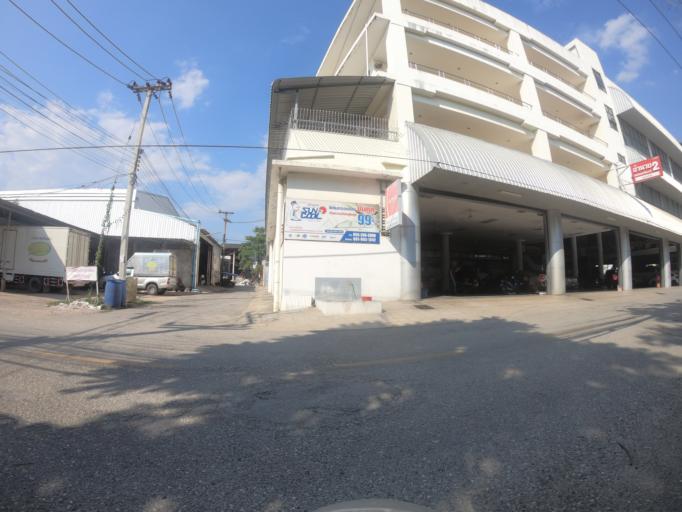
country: TH
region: Chiang Mai
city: Chiang Mai
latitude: 18.7890
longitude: 99.0241
